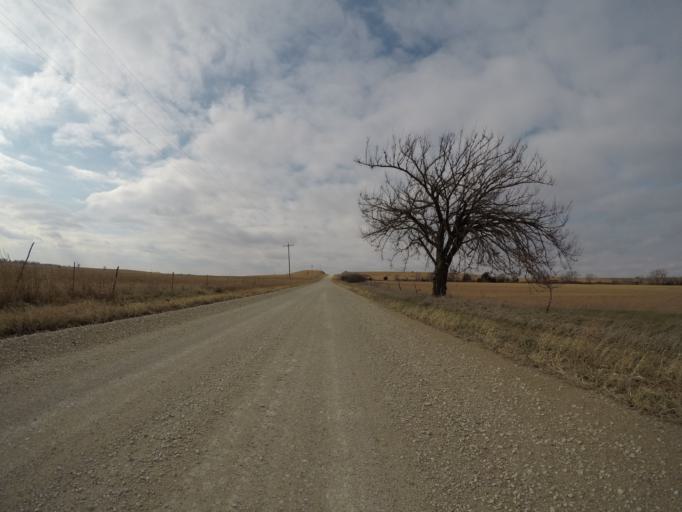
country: US
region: Kansas
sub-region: Morris County
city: Council Grove
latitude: 38.7680
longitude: -96.3187
